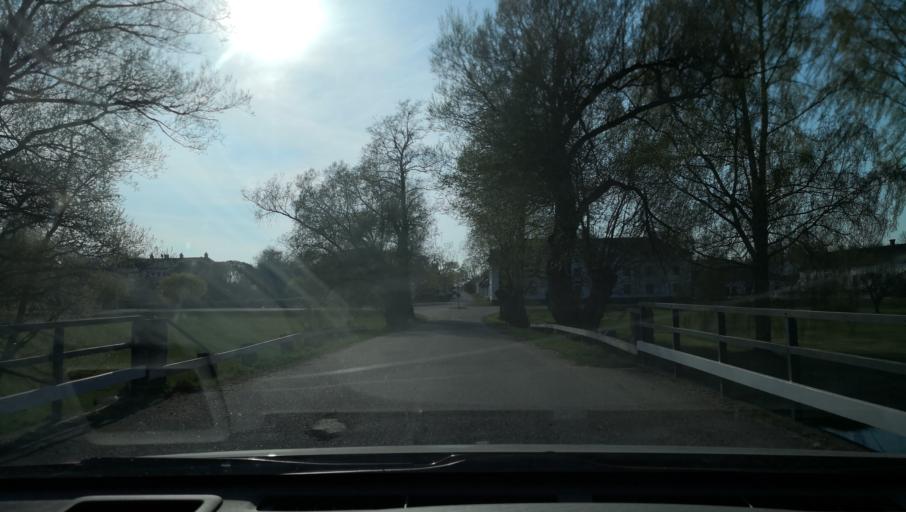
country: SE
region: Uppsala
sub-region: Heby Kommun
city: Tarnsjo
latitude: 60.2889
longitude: 16.8876
